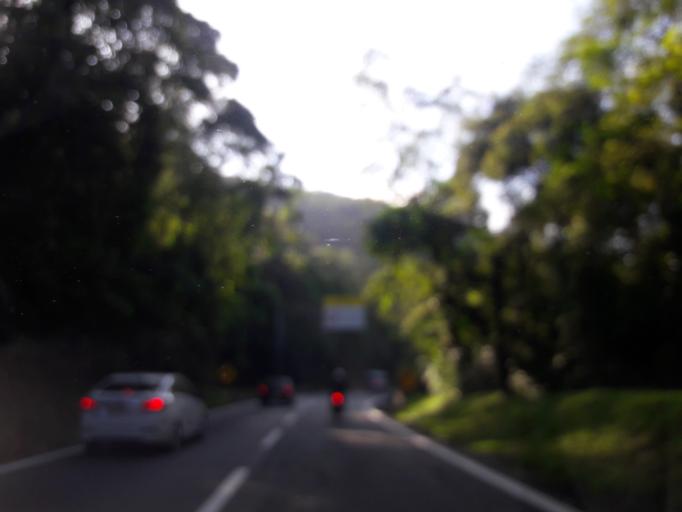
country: BR
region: Sao Paulo
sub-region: Cubatao
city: Cubatao
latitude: -23.8810
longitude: -46.4874
